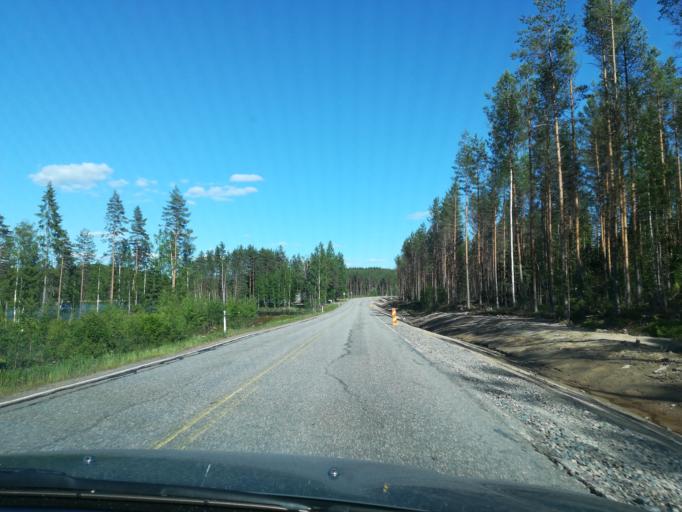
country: FI
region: Southern Savonia
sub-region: Mikkeli
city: Puumala
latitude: 61.4644
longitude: 28.3848
